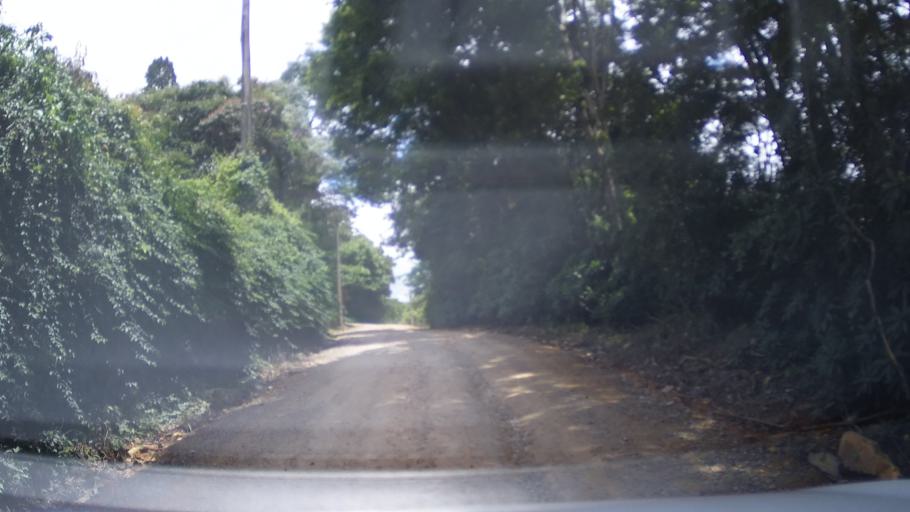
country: BR
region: Sao Paulo
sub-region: Vinhedo
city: Vinhedo
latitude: -22.9977
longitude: -46.9614
